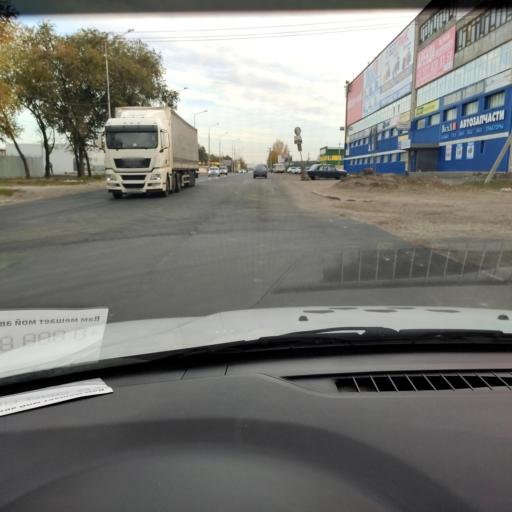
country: RU
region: Samara
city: Tol'yatti
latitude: 53.5684
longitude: 49.4583
